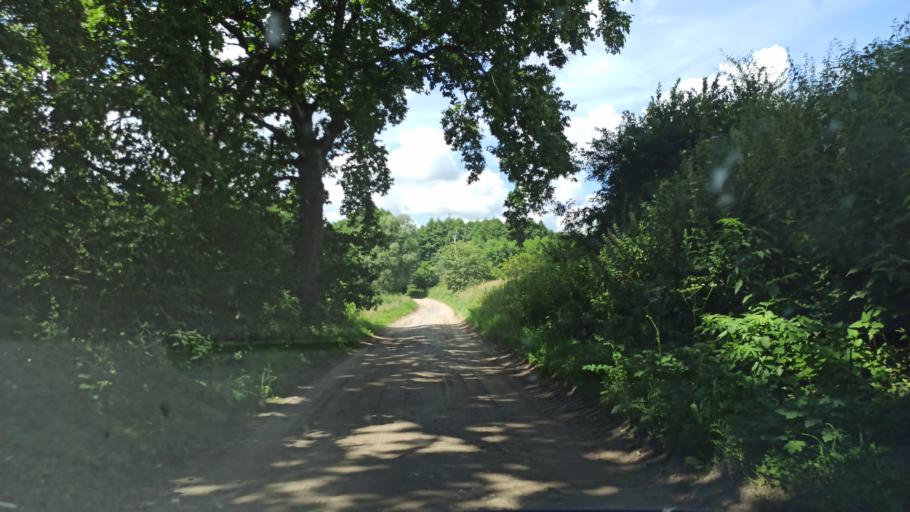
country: PL
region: Warmian-Masurian Voivodeship
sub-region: Powiat ostrodzki
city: Morag
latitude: 53.8665
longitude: 20.0570
